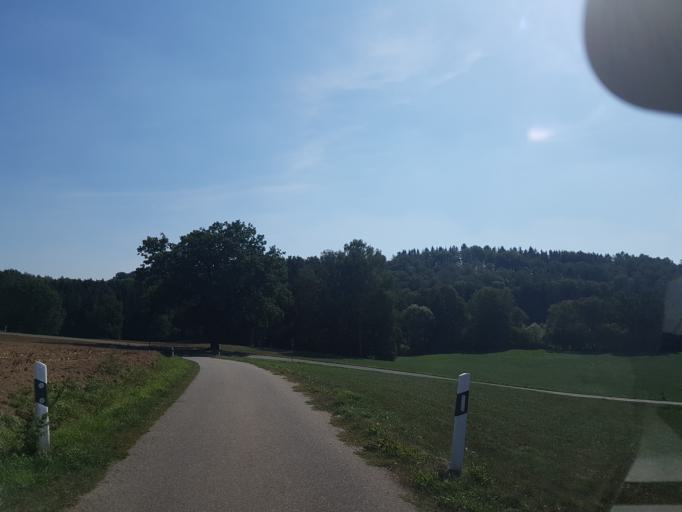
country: DE
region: Saxony
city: Kriebstein
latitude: 51.0497
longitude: 12.9849
